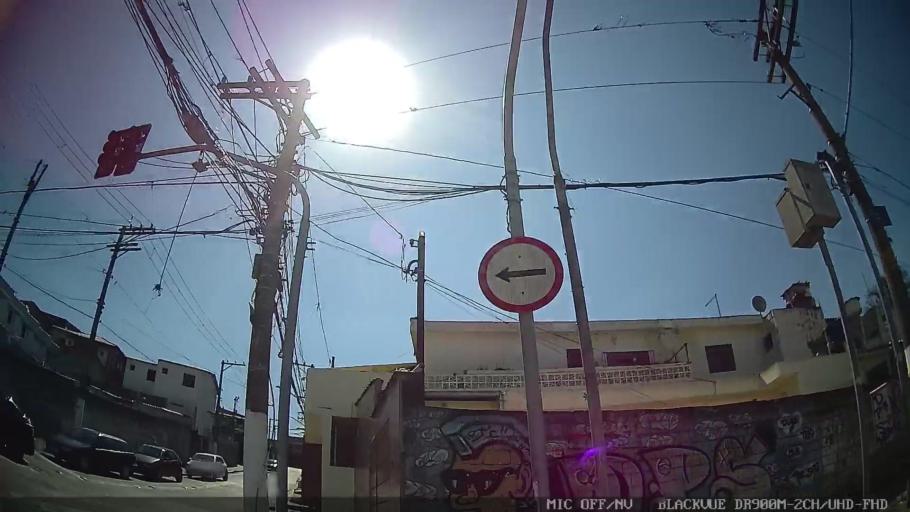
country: BR
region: Sao Paulo
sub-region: Sao Caetano Do Sul
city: Sao Caetano do Sul
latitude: -23.5898
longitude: -46.4949
